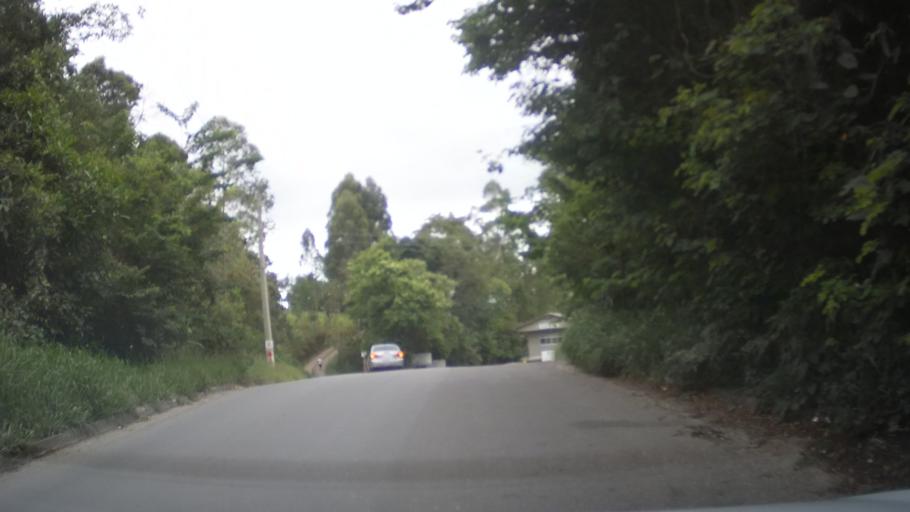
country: BR
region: Sao Paulo
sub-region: Aruja
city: Aruja
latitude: -23.3584
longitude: -46.2887
